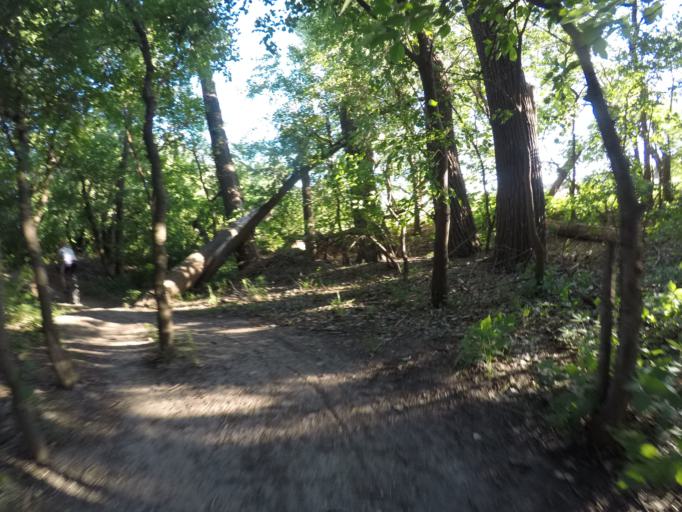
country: US
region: Kansas
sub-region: Riley County
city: Manhattan
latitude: 39.1869
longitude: -96.5325
